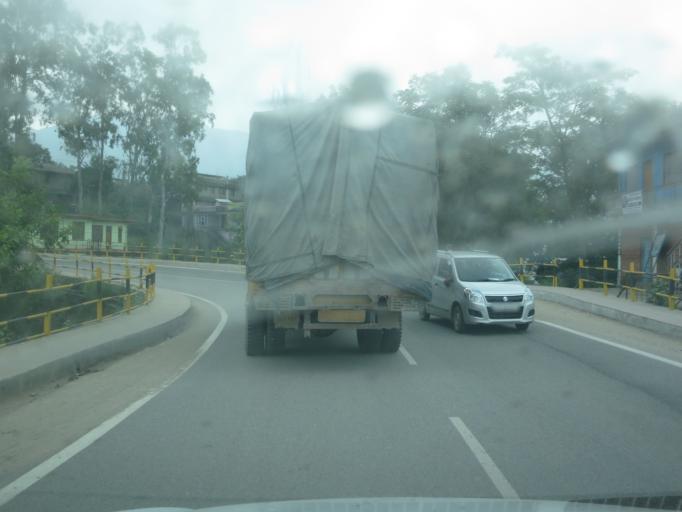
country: IN
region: Himachal Pradesh
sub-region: Mandi
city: Sundarnagar
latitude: 31.5174
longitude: 76.8824
